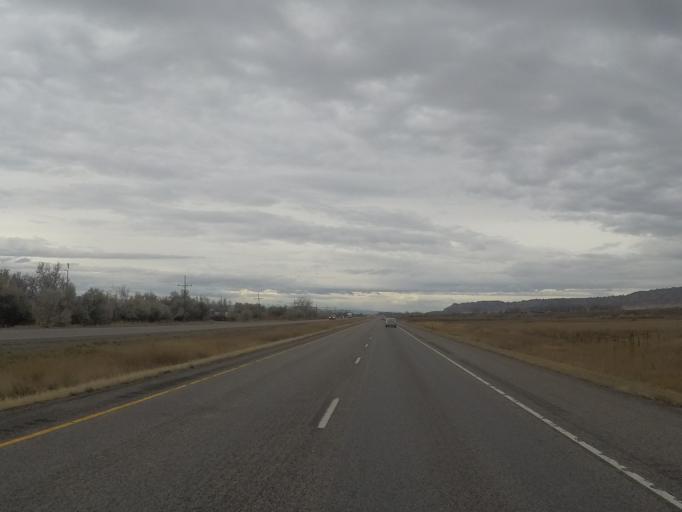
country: US
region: Montana
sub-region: Yellowstone County
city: Laurel
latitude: 45.6482
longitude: -108.8588
